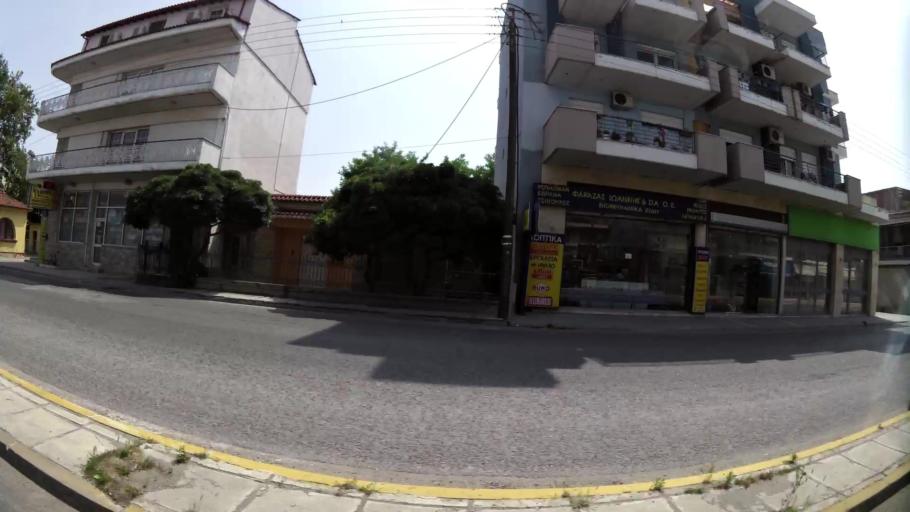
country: GR
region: Central Macedonia
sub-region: Nomos Thessalonikis
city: Diavata
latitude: 40.6861
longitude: 22.8552
